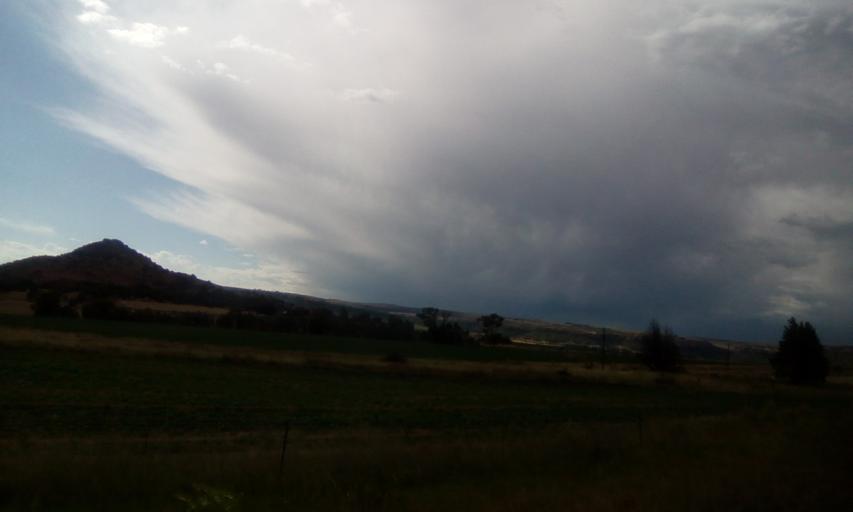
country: ZA
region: Orange Free State
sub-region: Thabo Mofutsanyana District Municipality
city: Ladybrand
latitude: -29.2561
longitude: 27.4332
